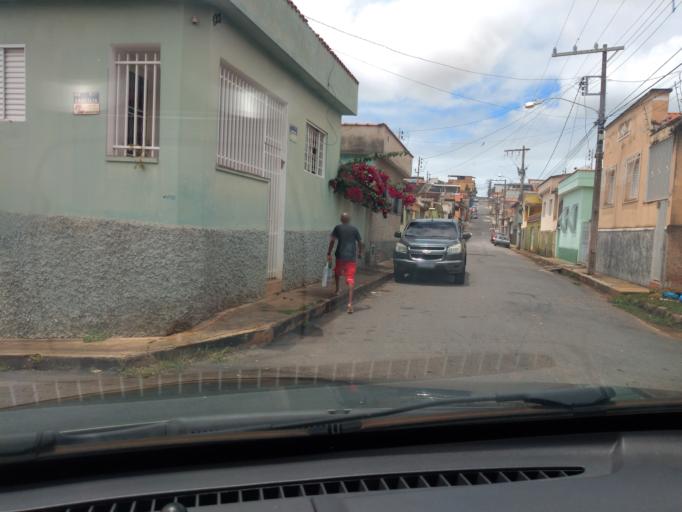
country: BR
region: Minas Gerais
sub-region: Tres Coracoes
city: Tres Coracoes
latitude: -21.6911
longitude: -45.2533
